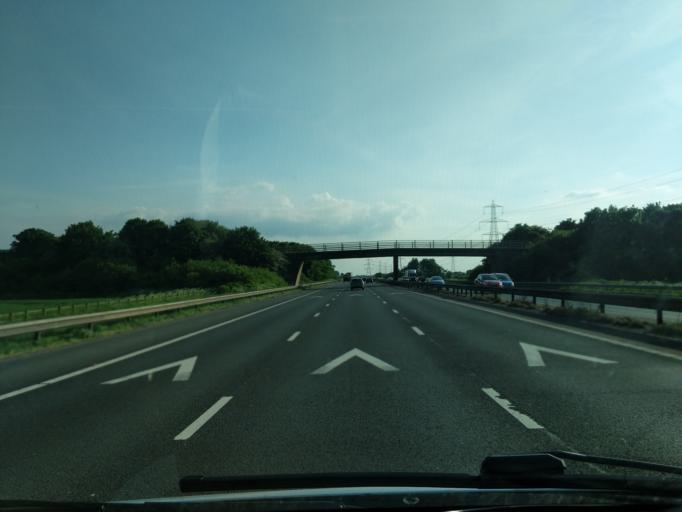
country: GB
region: England
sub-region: Cheshire West and Chester
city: Frodsham
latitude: 53.2905
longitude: -2.7463
